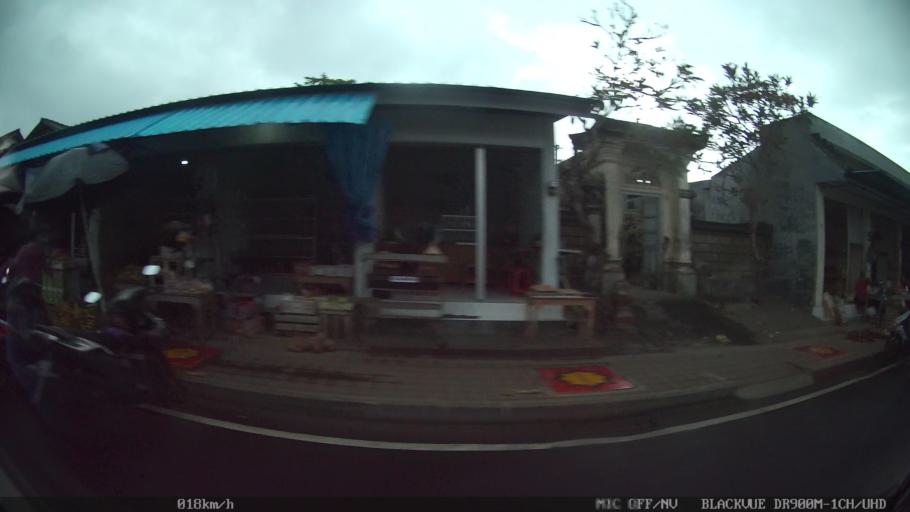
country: ID
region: Bali
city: Banjar Pasekan
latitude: -8.5946
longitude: 115.2804
